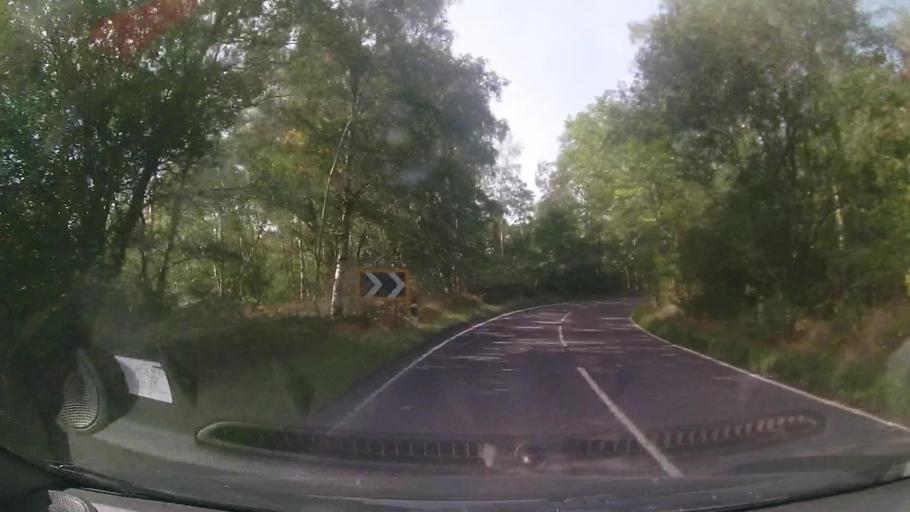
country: GB
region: England
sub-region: Shropshire
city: Lydham
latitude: 52.5332
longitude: -3.0001
